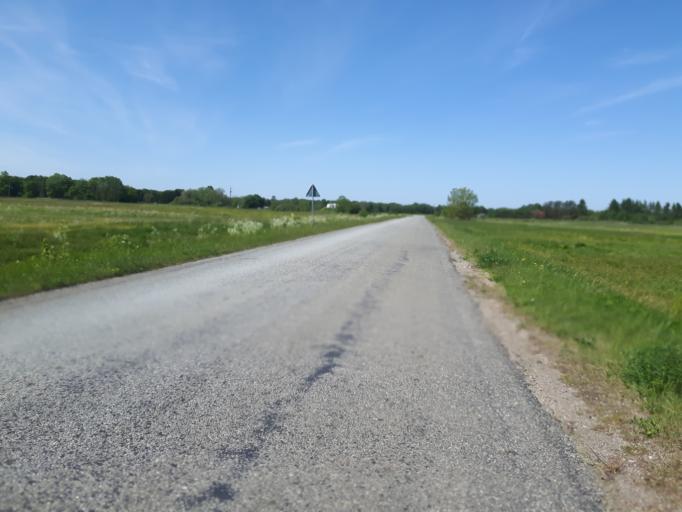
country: EE
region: Ida-Virumaa
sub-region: Aseri vald
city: Aseri
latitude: 59.4750
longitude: 26.7901
